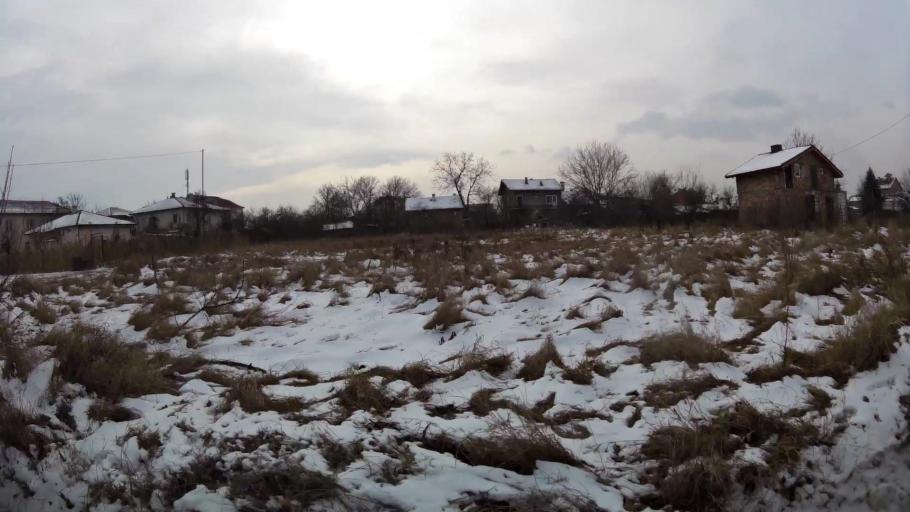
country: BG
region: Sofia-Capital
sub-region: Stolichna Obshtina
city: Sofia
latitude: 42.7100
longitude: 23.4136
